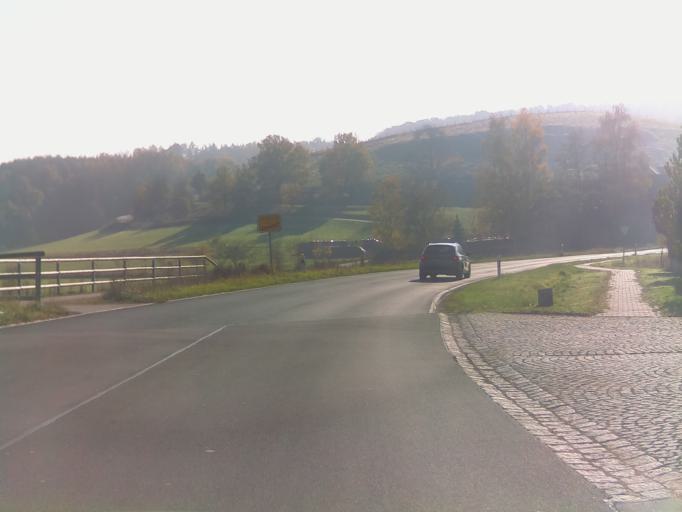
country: DE
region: Bavaria
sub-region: Upper Franconia
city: Burgwindheim
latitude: 49.8876
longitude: 10.5545
